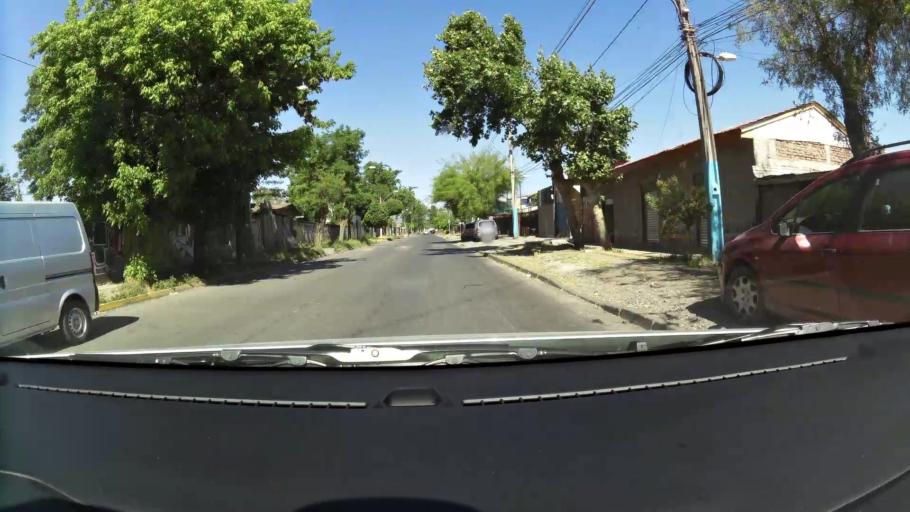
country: CL
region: Santiago Metropolitan
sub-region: Provincia de Maipo
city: San Bernardo
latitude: -33.5884
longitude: -70.6768
